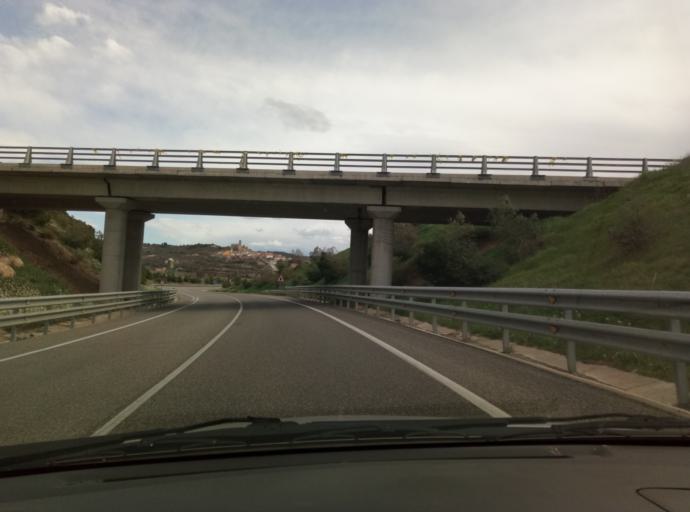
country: ES
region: Catalonia
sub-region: Provincia de Lleida
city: Ciutadilla
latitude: 41.5693
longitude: 1.1267
